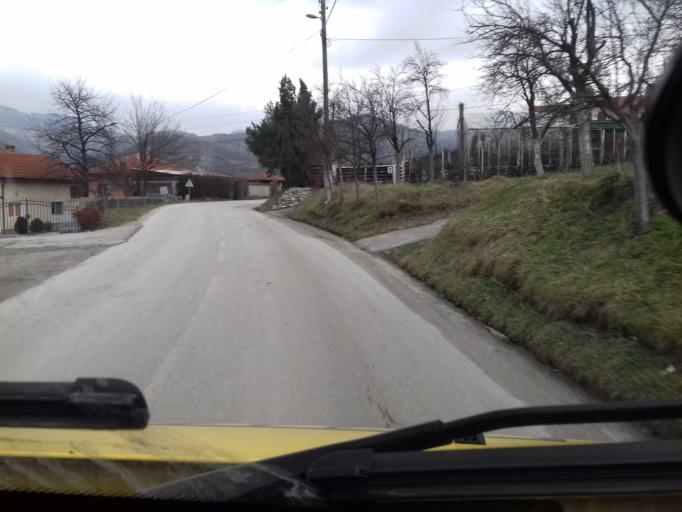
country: BA
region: Federation of Bosnia and Herzegovina
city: Zenica
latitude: 44.1802
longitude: 17.9639
